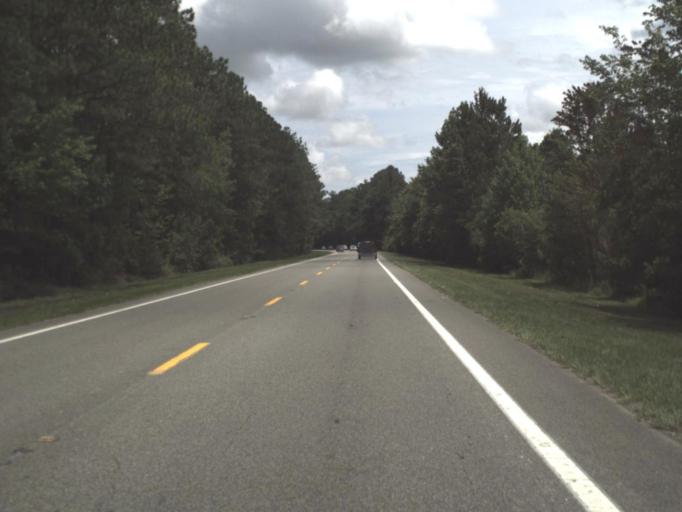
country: US
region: Florida
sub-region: Nassau County
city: Yulee
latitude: 30.6537
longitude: -81.6266
